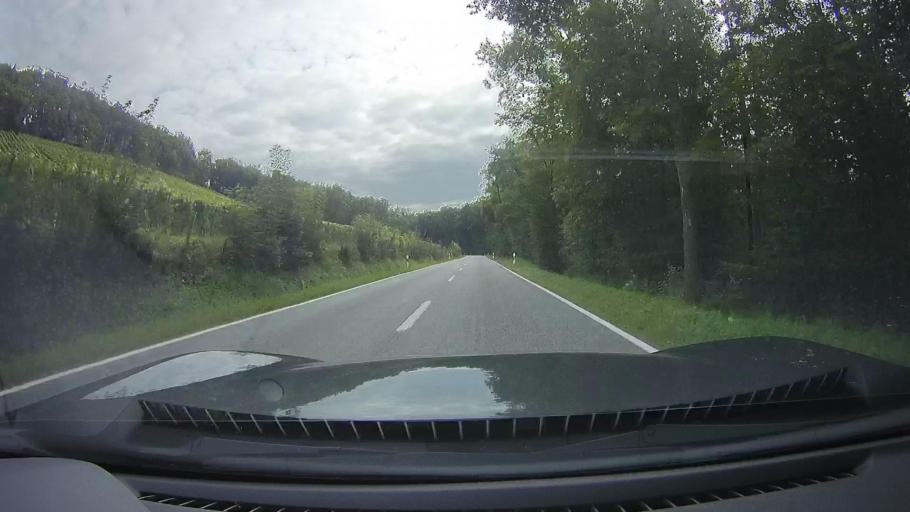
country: DE
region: Baden-Wuerttemberg
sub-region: Regierungsbezirk Stuttgart
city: Lowenstein
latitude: 49.0865
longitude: 9.3638
